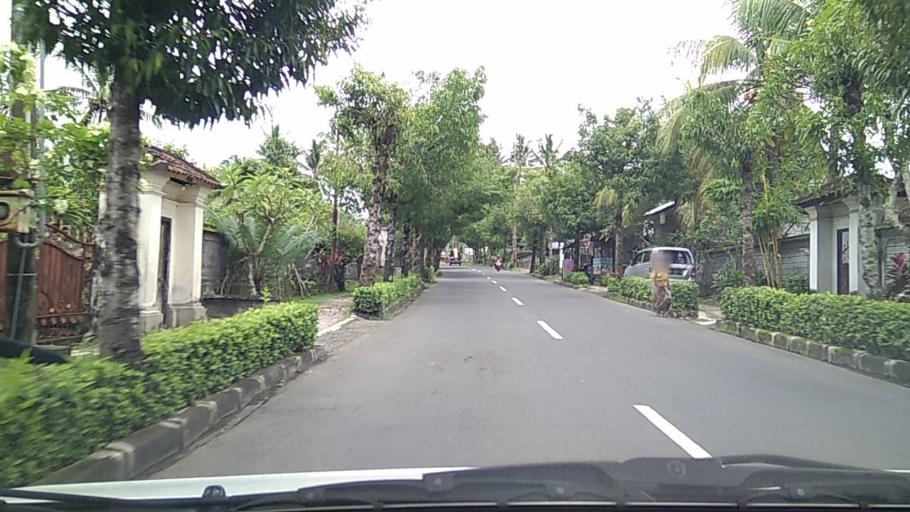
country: ID
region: Bali
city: Banjar Kelodan
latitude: -8.5283
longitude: 115.3481
